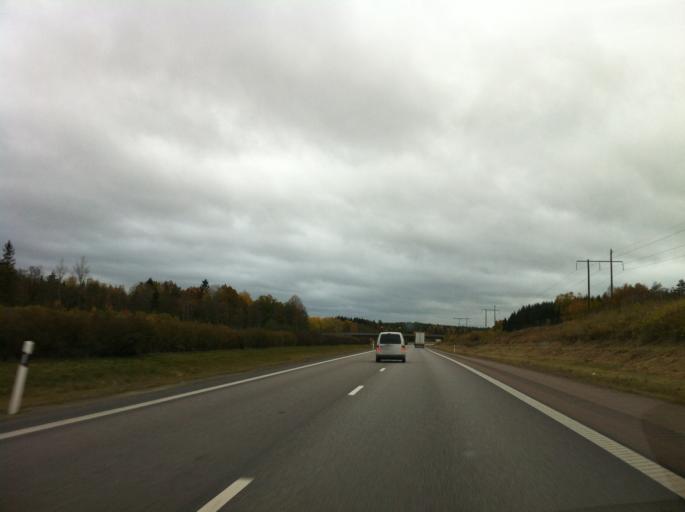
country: SE
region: OEstergoetland
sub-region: Vadstena Kommun
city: Herrestad
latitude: 58.2768
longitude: 14.8657
